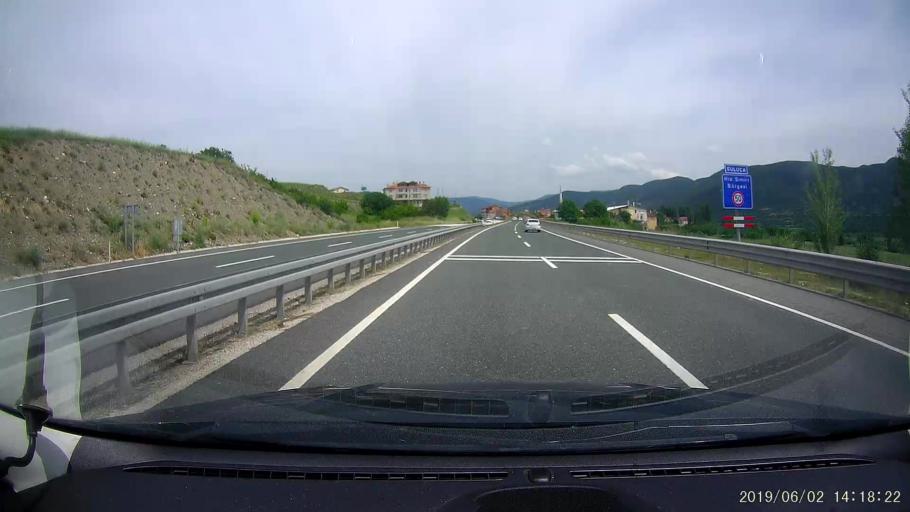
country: TR
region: Kastamonu
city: Tosya
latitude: 40.9573
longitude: 33.9539
